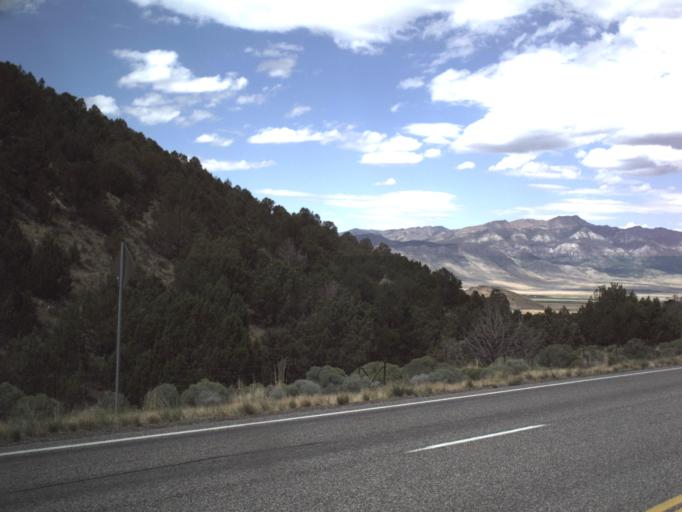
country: US
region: Utah
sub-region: Sanpete County
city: Gunnison
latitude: 39.1914
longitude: -112.0793
